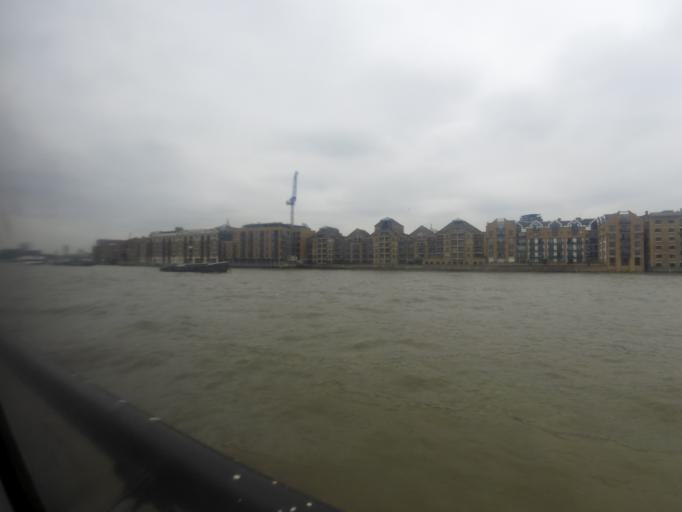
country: GB
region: England
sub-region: Greater London
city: Bethnal Green
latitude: 51.5042
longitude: -0.0528
